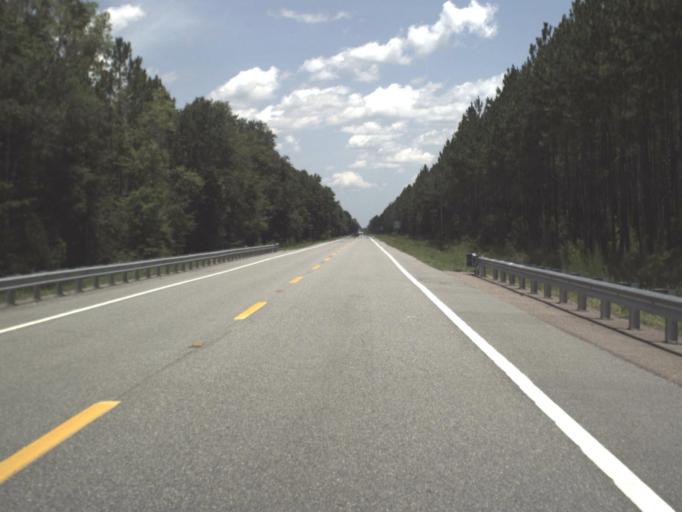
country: US
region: Florida
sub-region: Taylor County
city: Steinhatchee
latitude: 29.8211
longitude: -83.3158
